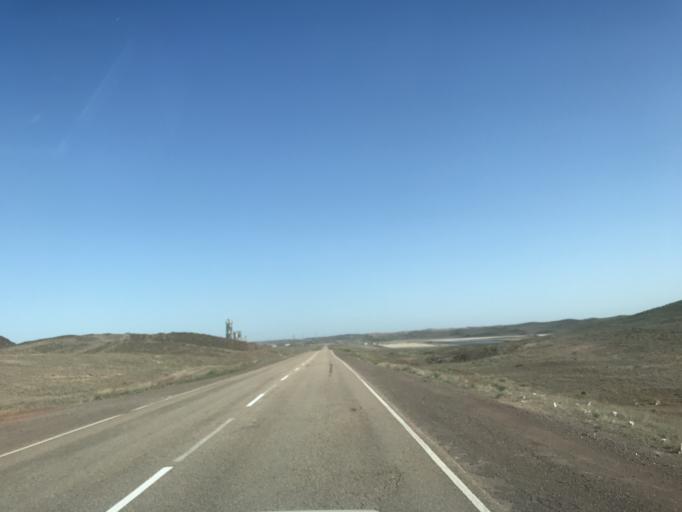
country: KZ
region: Zhambyl
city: Mynaral
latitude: 45.4026
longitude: 73.6365
